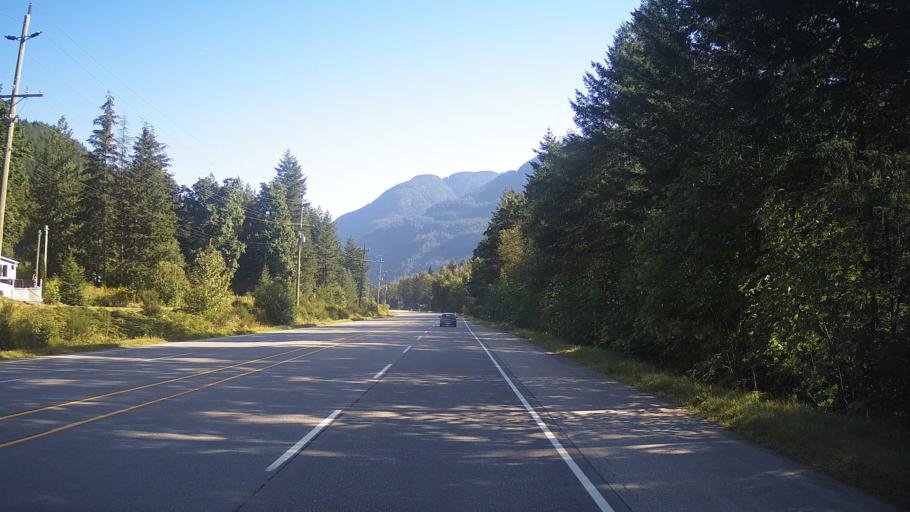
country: CA
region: British Columbia
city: Hope
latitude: 49.4771
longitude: -121.4248
